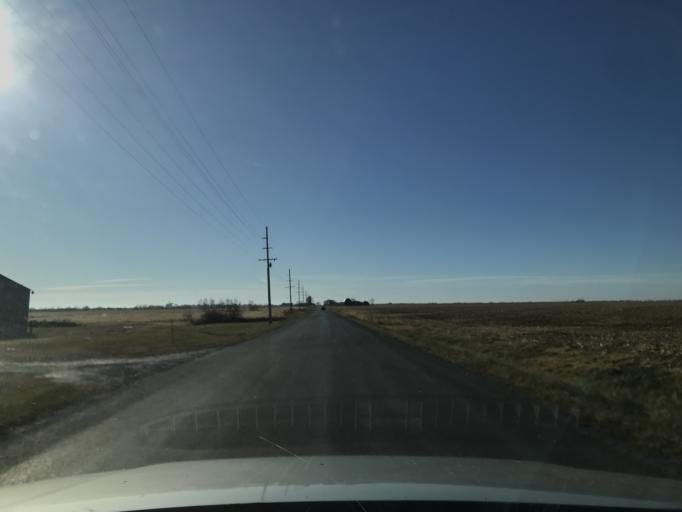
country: US
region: Illinois
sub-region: Hancock County
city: Carthage
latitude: 40.4993
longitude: -91.1778
